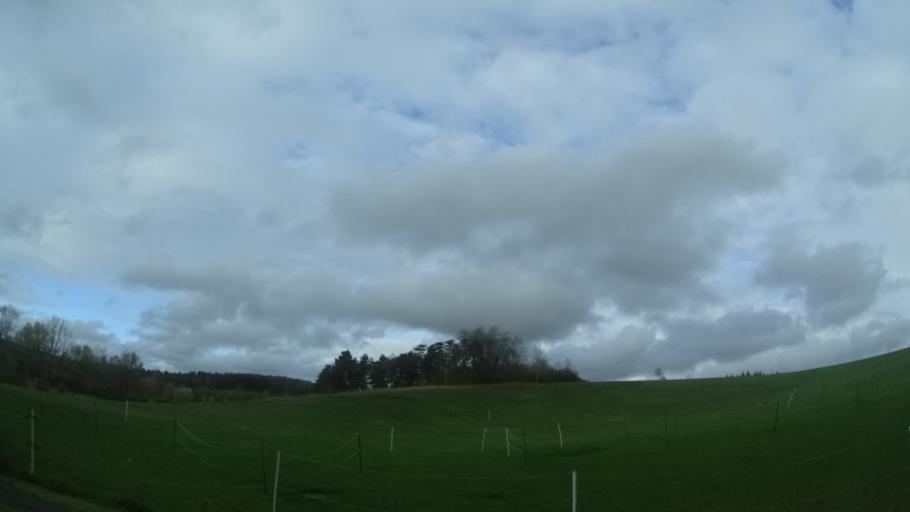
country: DE
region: Thuringia
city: Romhild
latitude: 50.3912
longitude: 10.4920
